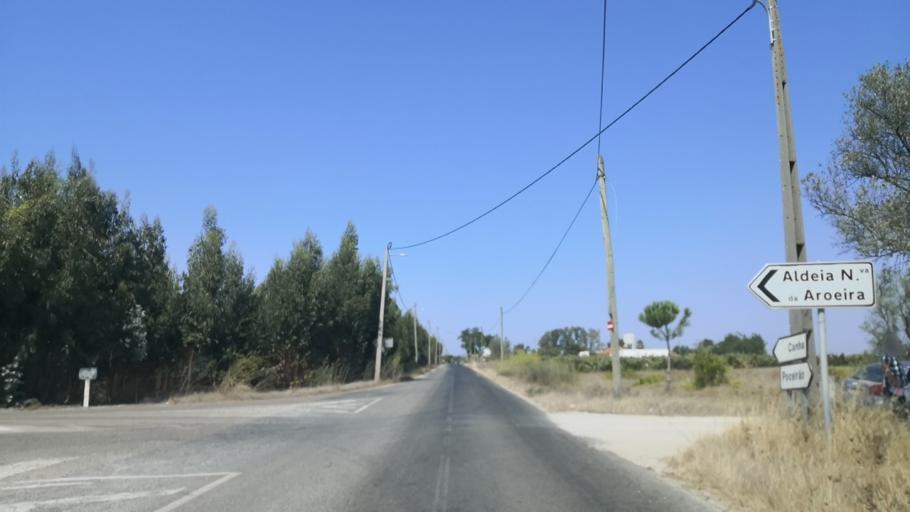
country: PT
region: Santarem
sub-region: Benavente
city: Poceirao
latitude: 38.7137
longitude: -8.7146
